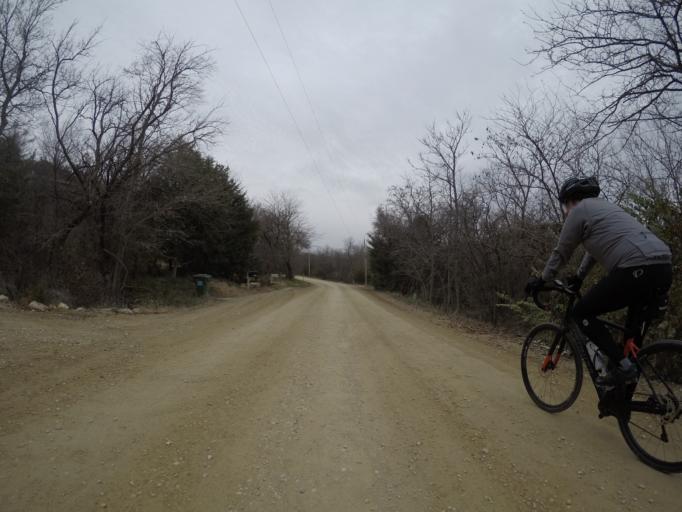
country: US
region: Kansas
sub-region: Riley County
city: Ogden
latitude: 39.1713
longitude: -96.6800
